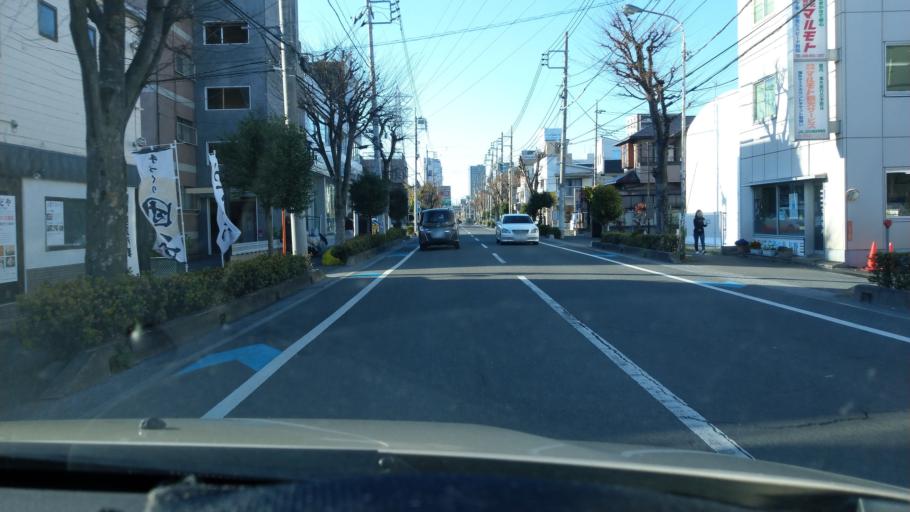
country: JP
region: Saitama
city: Yono
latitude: 35.8941
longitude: 139.6224
